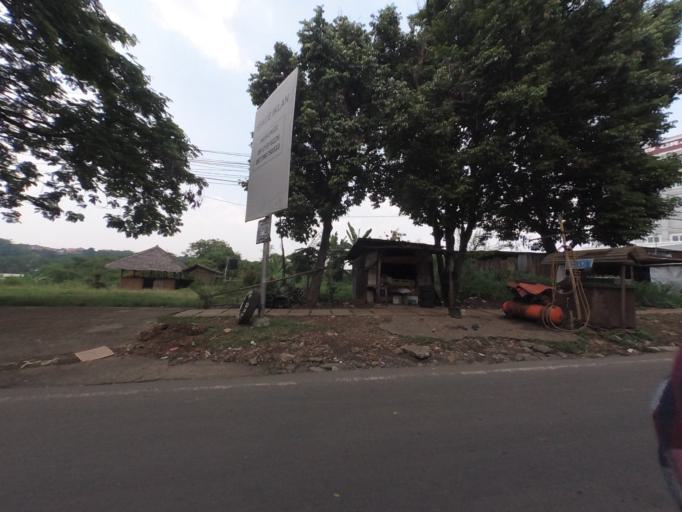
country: ID
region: West Java
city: Bogor
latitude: -6.5666
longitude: 106.7615
